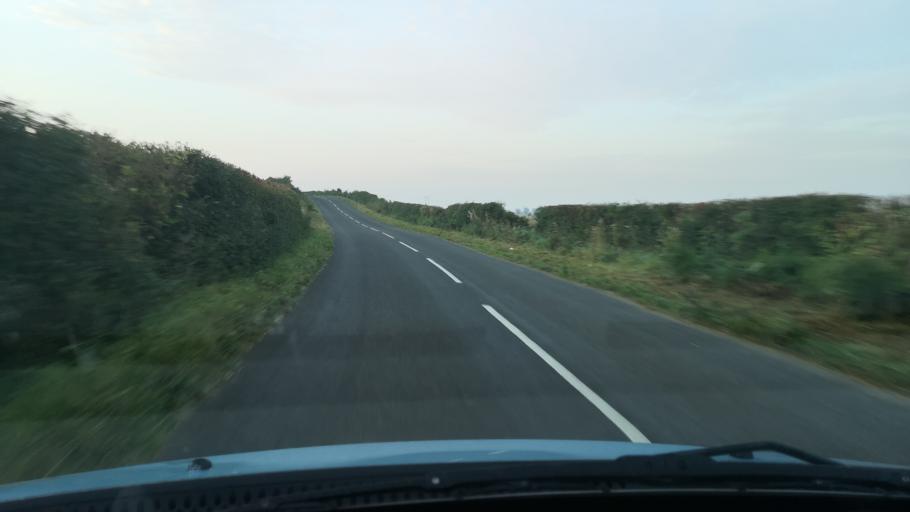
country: GB
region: England
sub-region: City and Borough of Wakefield
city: Darrington
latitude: 53.6647
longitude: -1.2871
